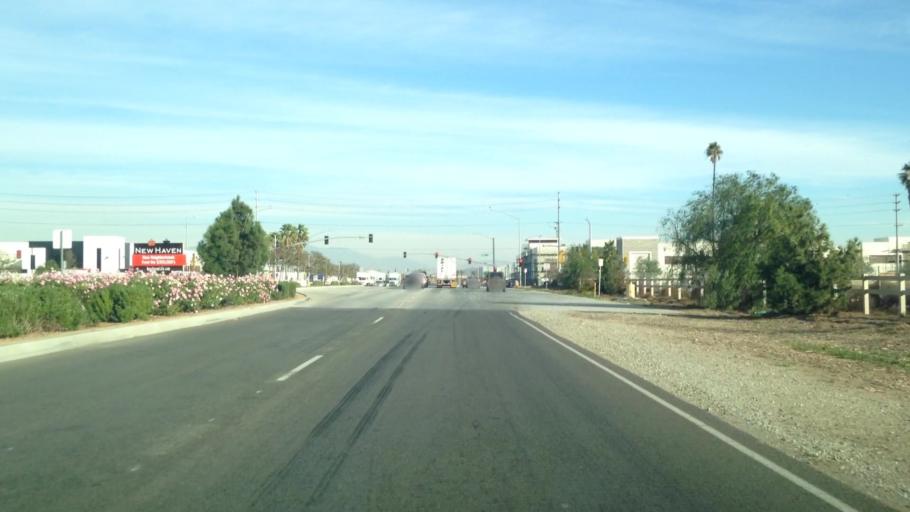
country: US
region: California
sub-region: Riverside County
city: Mira Loma
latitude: 34.0008
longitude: -117.5605
